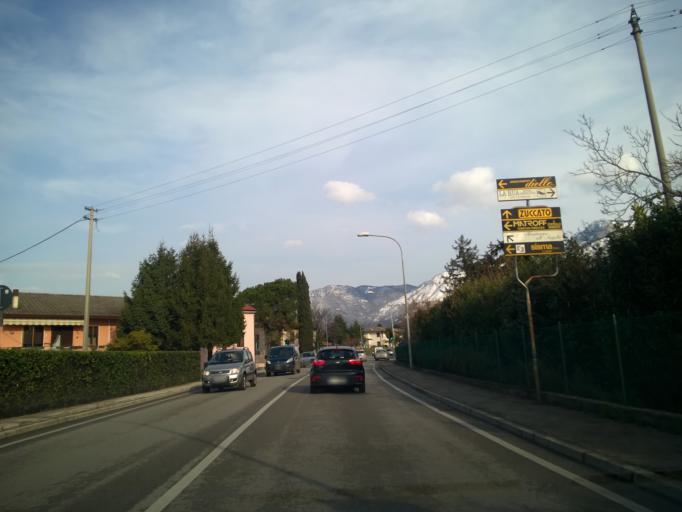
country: IT
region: Veneto
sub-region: Provincia di Vicenza
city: Carre
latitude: 45.7462
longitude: 11.4573
